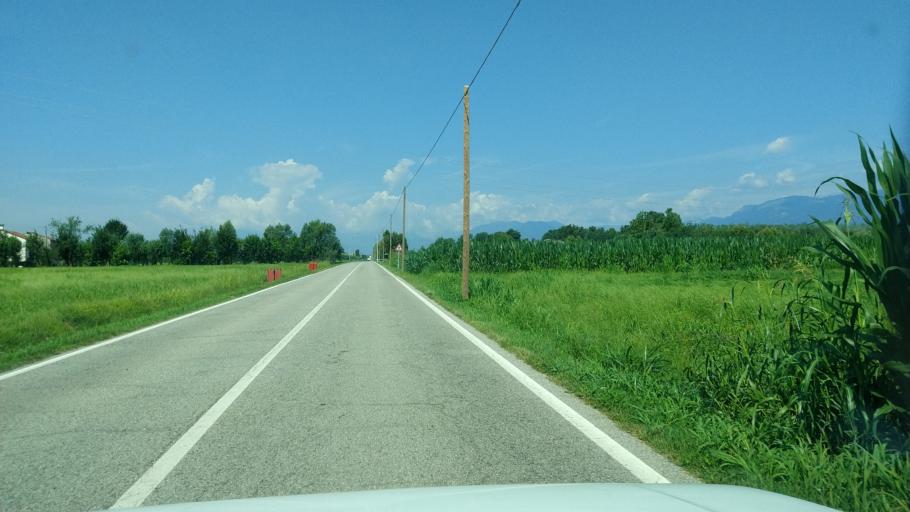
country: IT
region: Veneto
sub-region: Provincia di Vicenza
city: Schiavon
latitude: 45.6900
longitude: 11.6675
